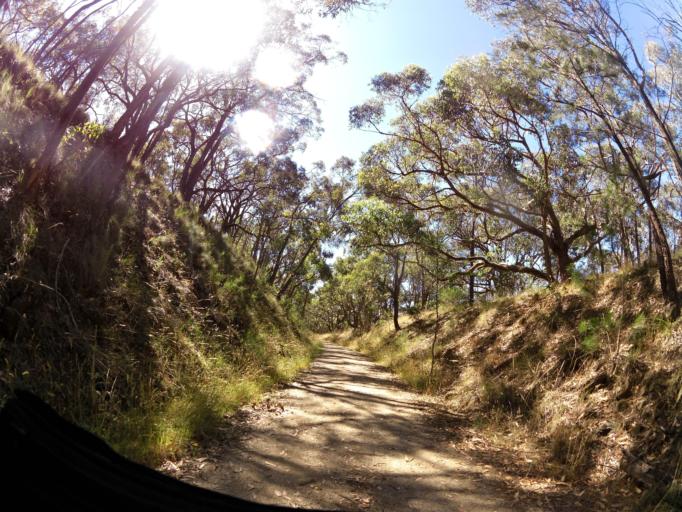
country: AU
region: Victoria
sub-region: Ballarat North
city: Delacombe
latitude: -37.6658
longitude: 143.5078
